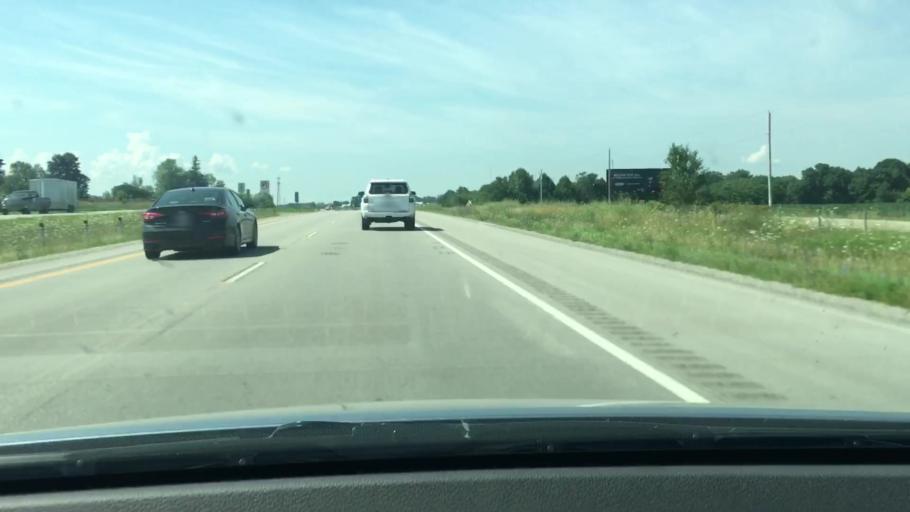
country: US
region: Wisconsin
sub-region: Brown County
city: Wrightstown
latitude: 44.3375
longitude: -88.2039
